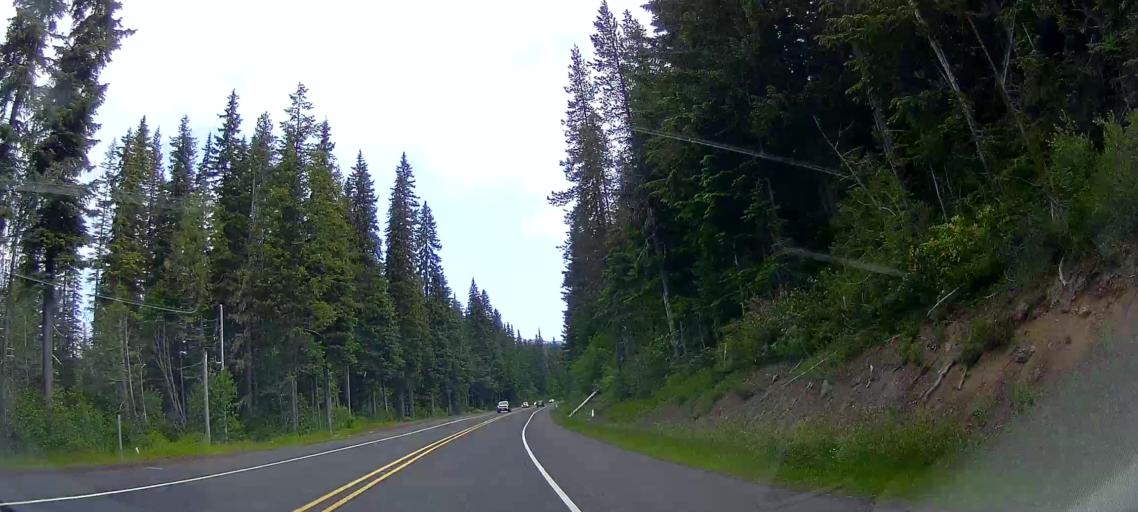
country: US
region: Oregon
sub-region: Clackamas County
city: Mount Hood Village
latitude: 45.2734
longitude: -121.7175
